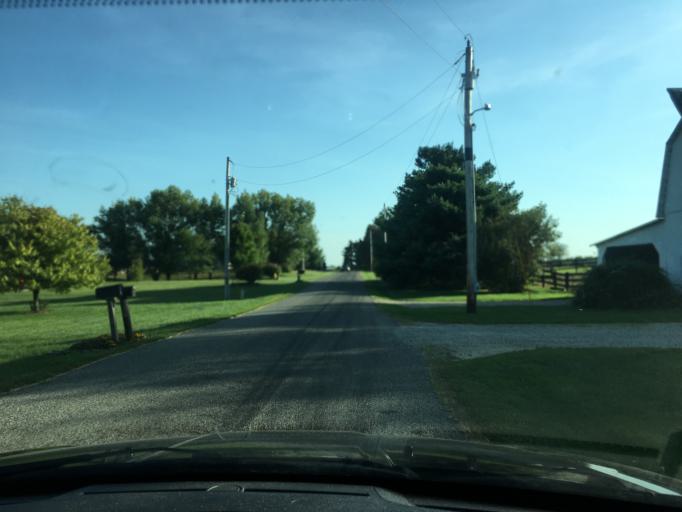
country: US
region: Ohio
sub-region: Logan County
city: West Liberty
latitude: 40.3014
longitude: -83.7458
